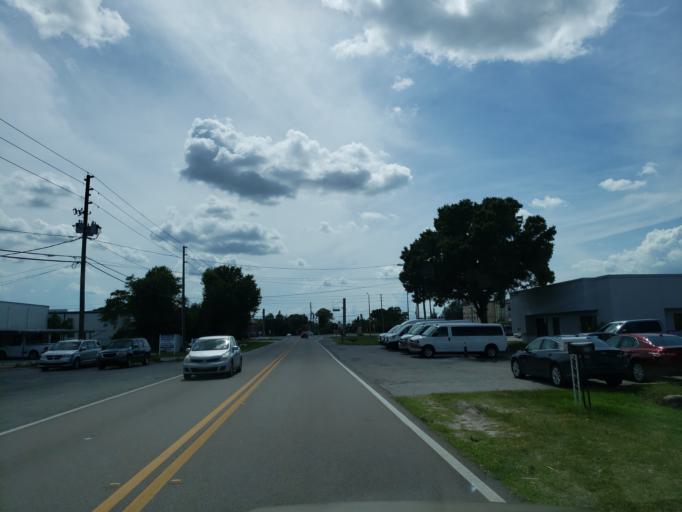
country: US
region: Florida
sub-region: Pinellas County
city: South Highpoint
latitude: 27.8865
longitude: -82.7273
